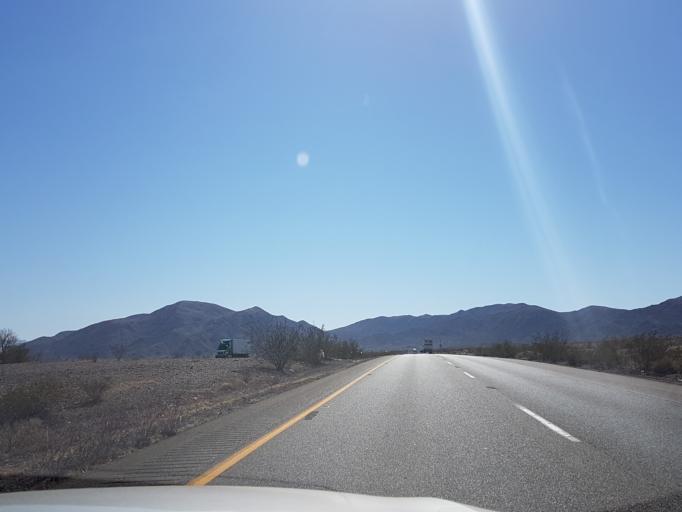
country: US
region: California
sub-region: San Bernardino County
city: Fort Irwin
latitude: 35.2112
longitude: -116.1147
